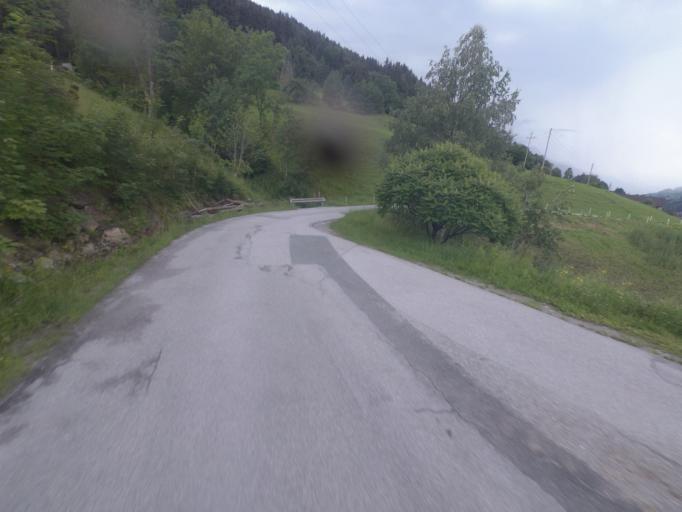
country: AT
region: Salzburg
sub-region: Politischer Bezirk Sankt Johann im Pongau
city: Schwarzach im Pongau
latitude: 47.3137
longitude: 13.1551
